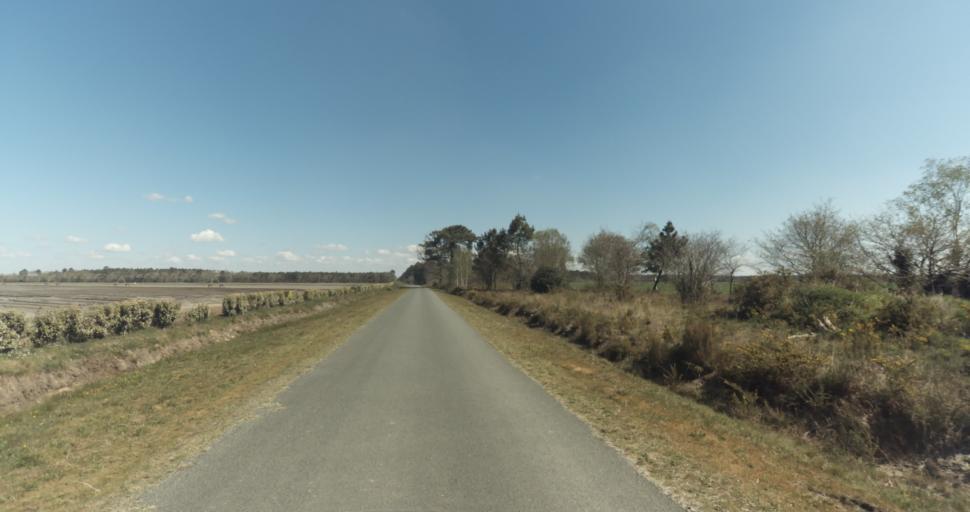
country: FR
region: Aquitaine
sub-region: Departement de la Gironde
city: Martignas-sur-Jalle
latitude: 44.7706
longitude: -0.8081
